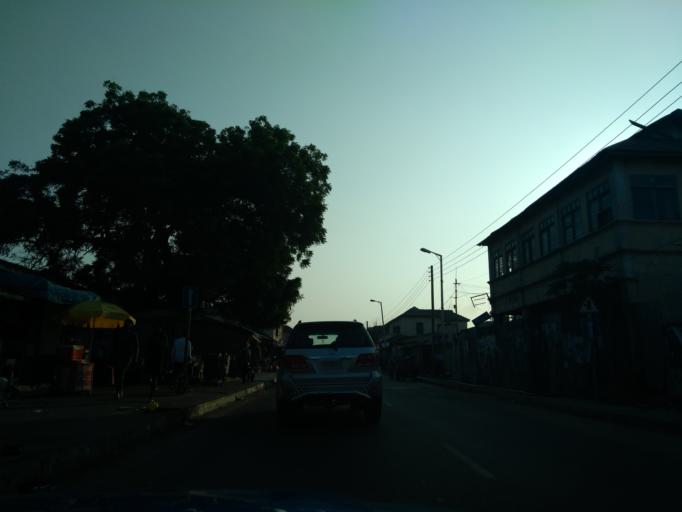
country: GH
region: Greater Accra
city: Accra
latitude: 5.5416
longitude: -0.2108
